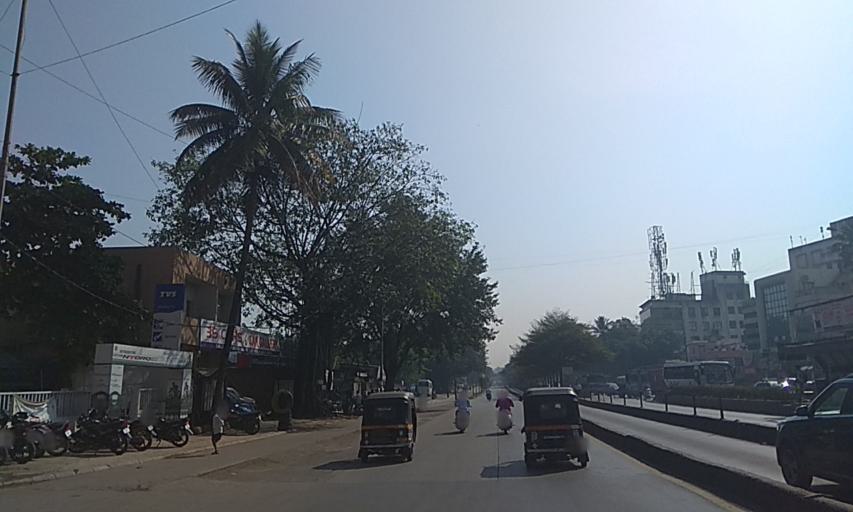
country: IN
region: Maharashtra
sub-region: Pune Division
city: Pune
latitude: 18.5040
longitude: 73.9220
